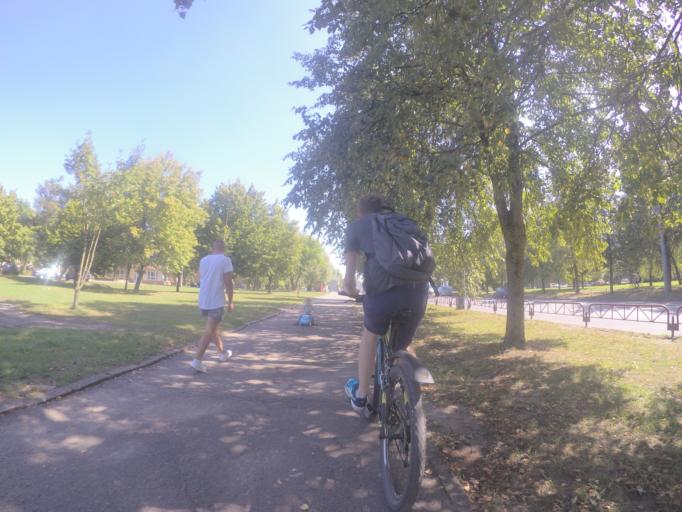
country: BY
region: Grodnenskaya
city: Hrodna
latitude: 53.6655
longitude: 23.7880
